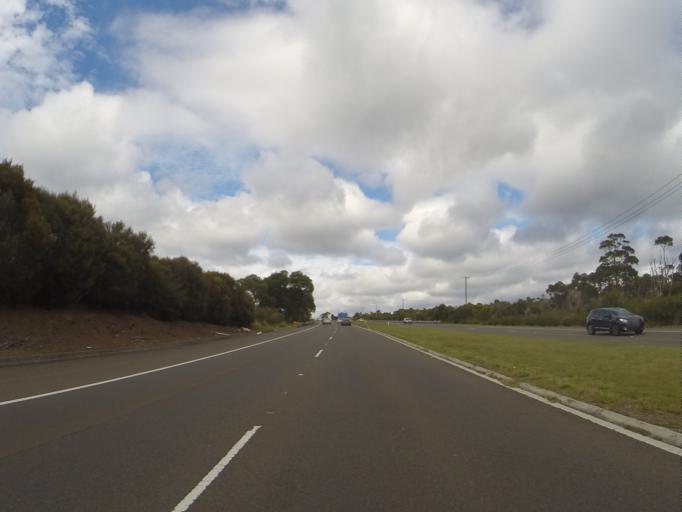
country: AU
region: New South Wales
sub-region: Sutherland Shire
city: Heathcote
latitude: -34.1019
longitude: 150.9947
